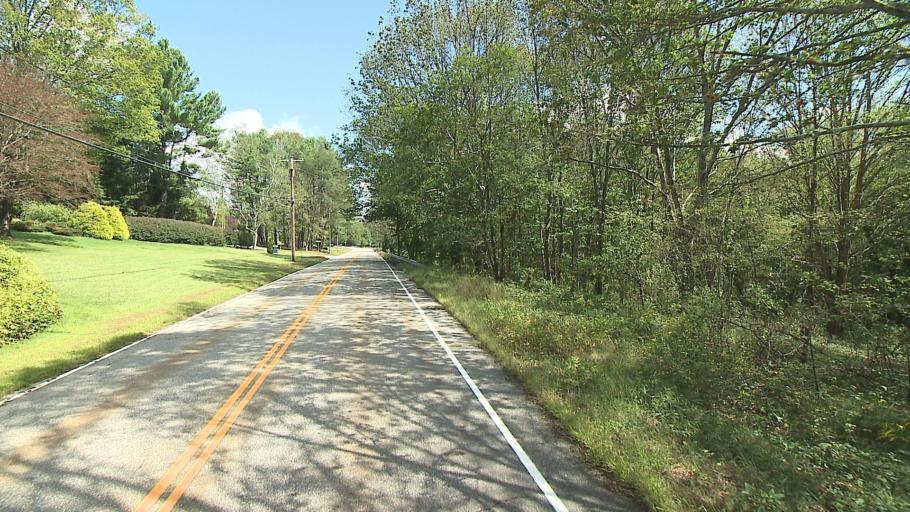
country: US
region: Connecticut
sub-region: Windham County
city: Putnam
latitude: 41.8641
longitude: -71.9636
